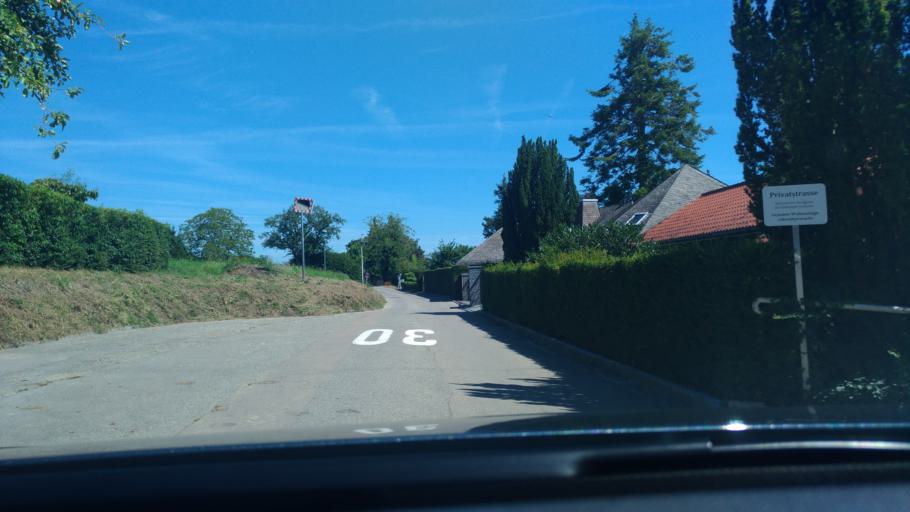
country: DE
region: Baden-Wuerttemberg
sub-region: Tuebingen Region
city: Uberlingen
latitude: 47.7719
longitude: 9.1431
